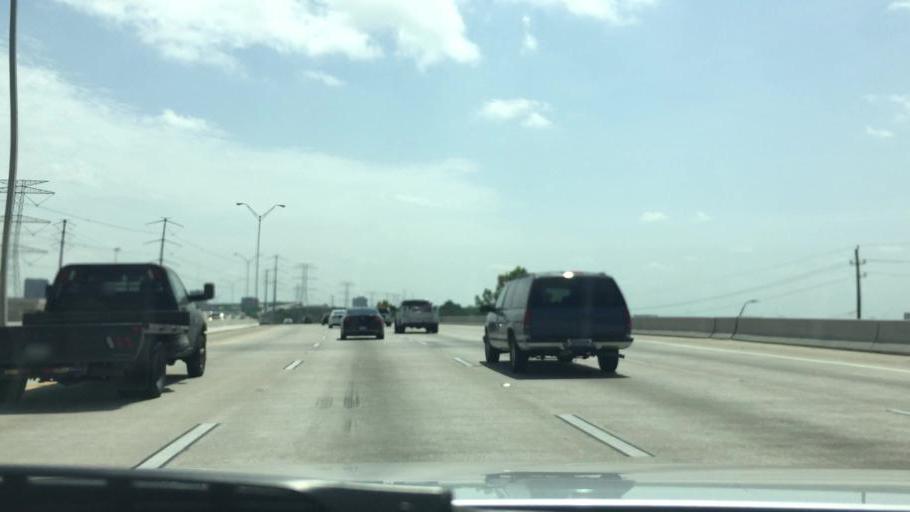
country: US
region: Texas
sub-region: Harris County
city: Aldine
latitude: 29.9376
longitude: -95.4328
